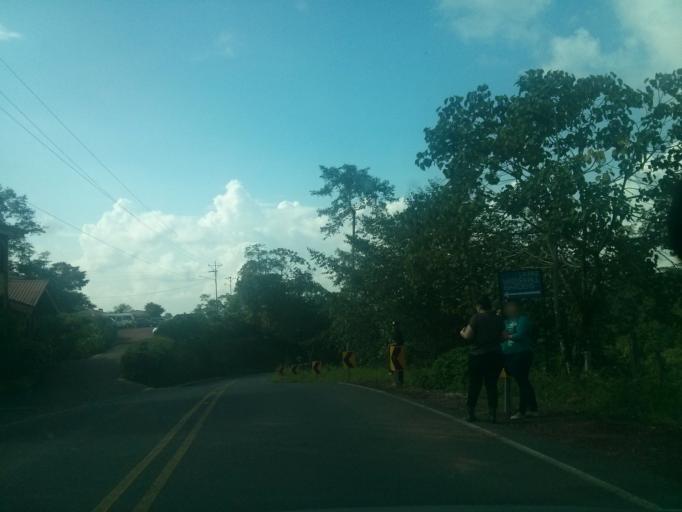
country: CR
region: Alajuela
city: Rio Segundo
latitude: 10.2041
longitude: -84.1612
